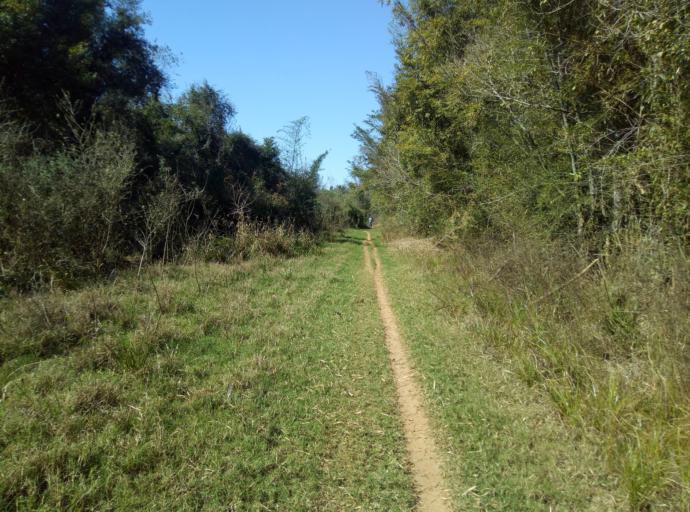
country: PY
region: Caaguazu
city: Doctor Cecilio Baez
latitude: -25.1792
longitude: -56.2237
